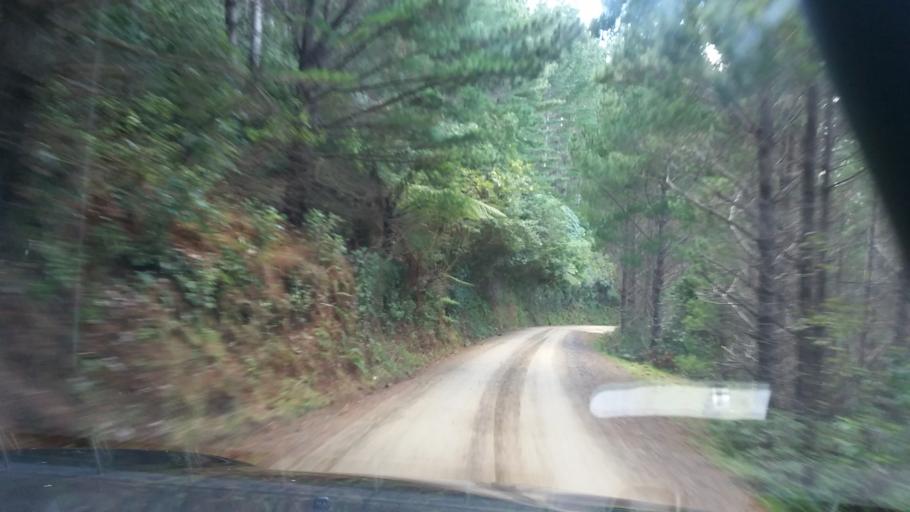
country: NZ
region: Marlborough
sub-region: Marlborough District
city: Picton
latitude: -40.9852
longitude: 173.8218
